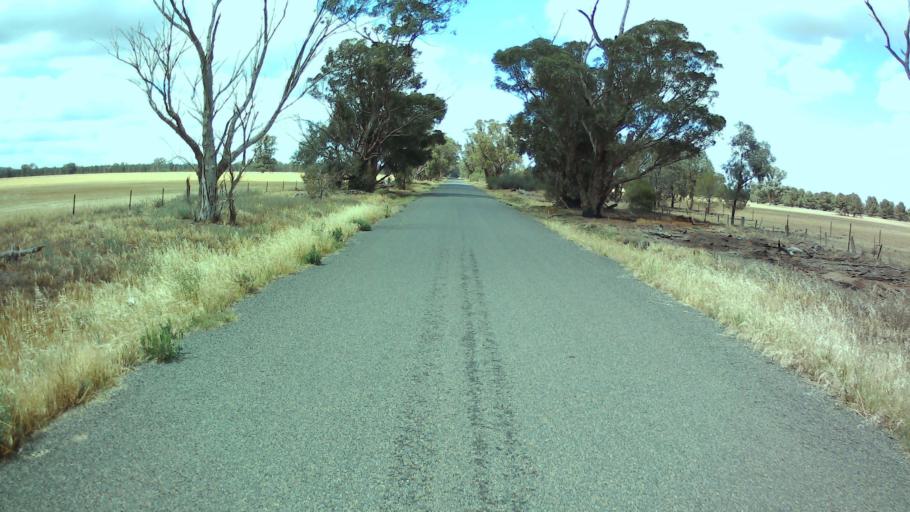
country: AU
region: New South Wales
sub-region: Weddin
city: Grenfell
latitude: -33.8887
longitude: 147.9230
